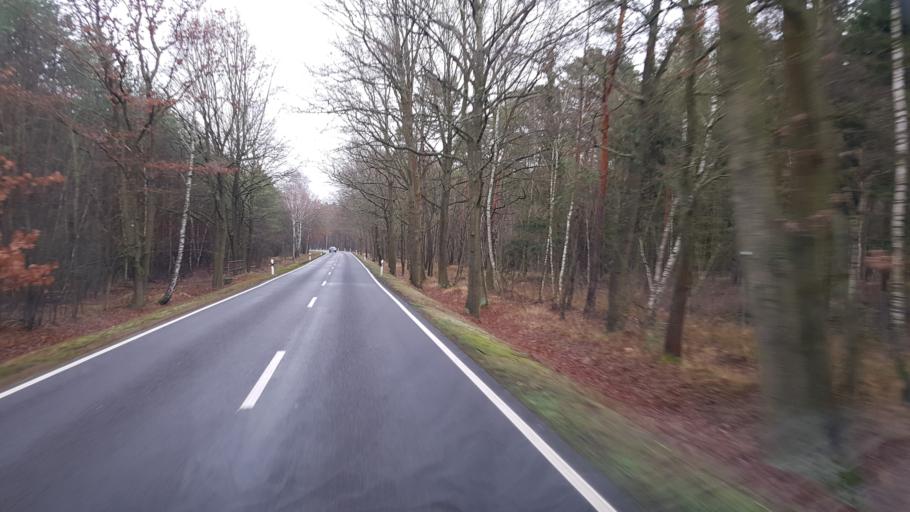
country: DE
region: Brandenburg
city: Altdobern
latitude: 51.6995
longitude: 14.0270
